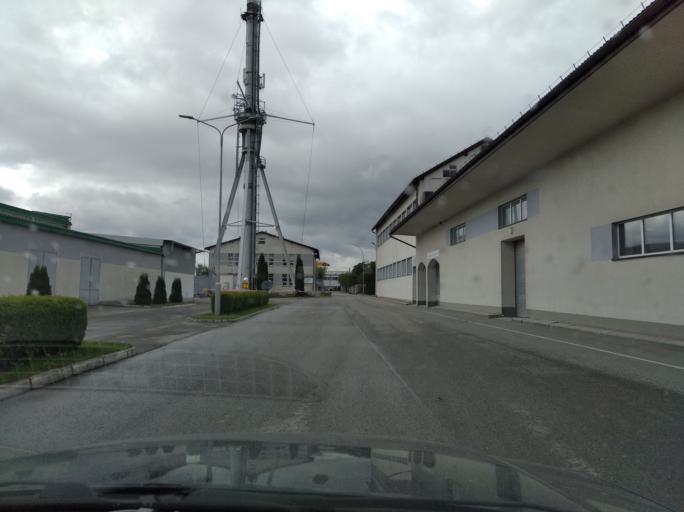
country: PL
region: Subcarpathian Voivodeship
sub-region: Powiat rzeszowski
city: Boguchwala
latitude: 49.9875
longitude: 21.9353
